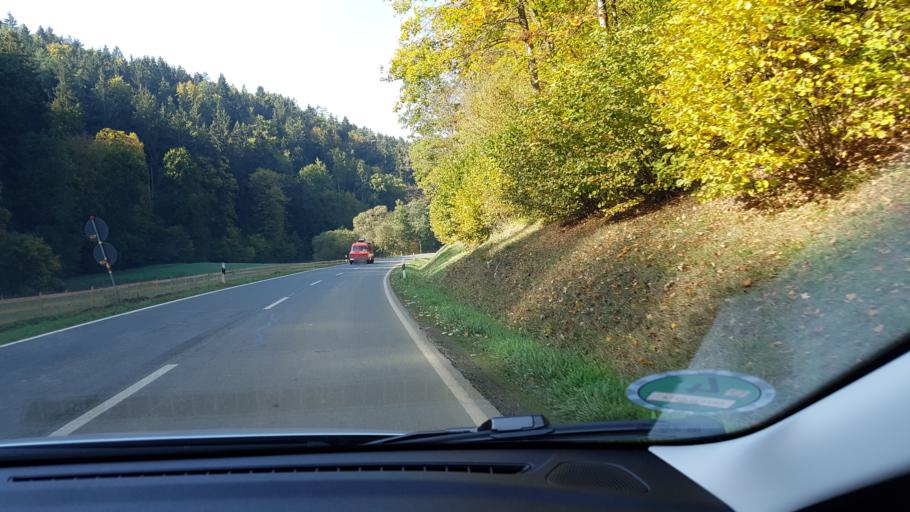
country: DE
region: Bavaria
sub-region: Upper Franconia
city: Waischenfeld
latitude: 49.8204
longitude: 11.3225
